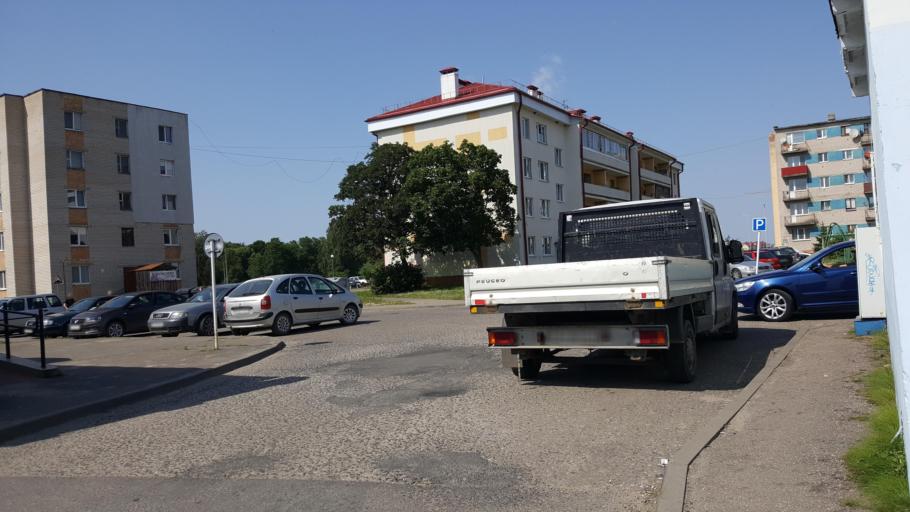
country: BY
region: Brest
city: Zhabinka
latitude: 52.1927
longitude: 24.0301
